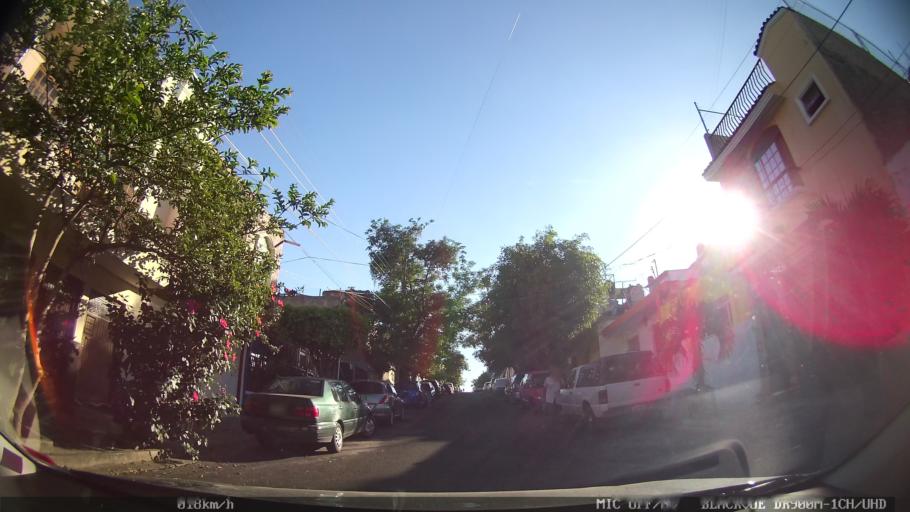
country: MX
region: Jalisco
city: Tlaquepaque
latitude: 20.7080
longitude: -103.2895
